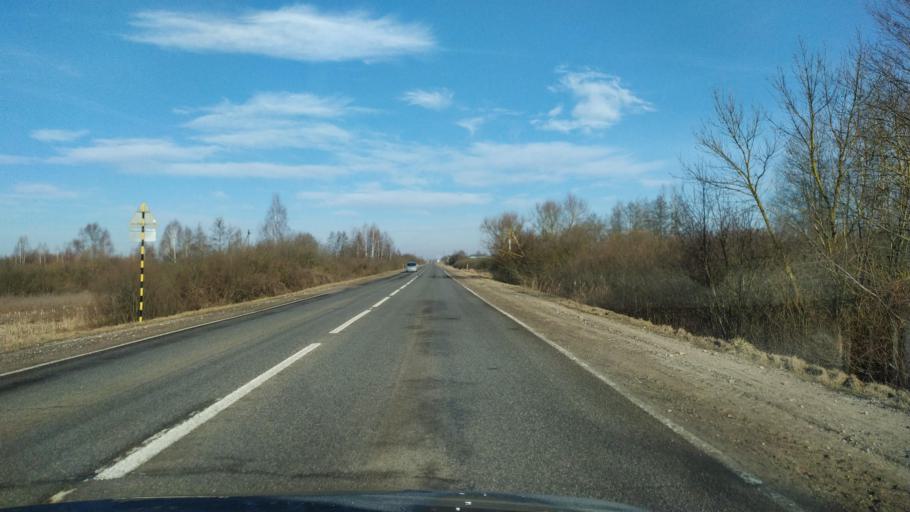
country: BY
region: Brest
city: Kamyanyets
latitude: 52.3879
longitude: 23.7872
